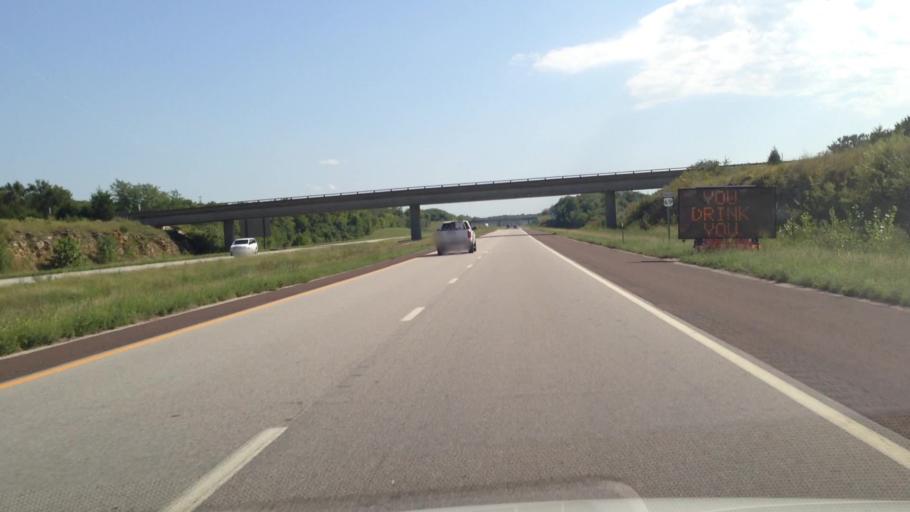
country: US
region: Kansas
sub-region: Miami County
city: Louisburg
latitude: 38.6151
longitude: -94.6950
